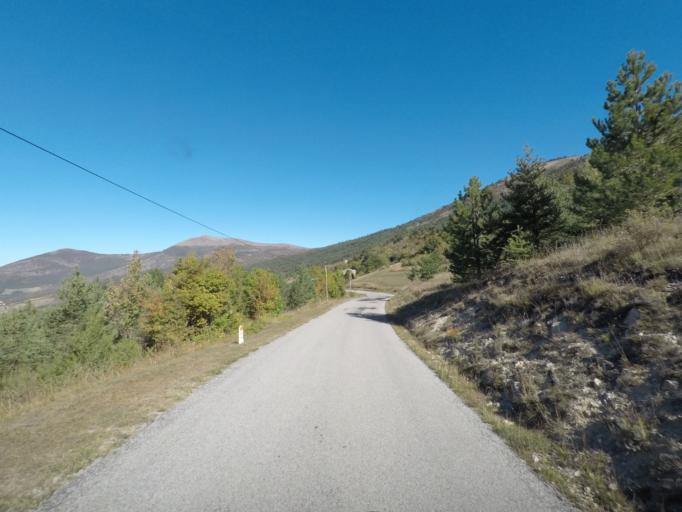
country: FR
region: Rhone-Alpes
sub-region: Departement de la Drome
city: Die
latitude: 44.5421
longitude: 5.3695
